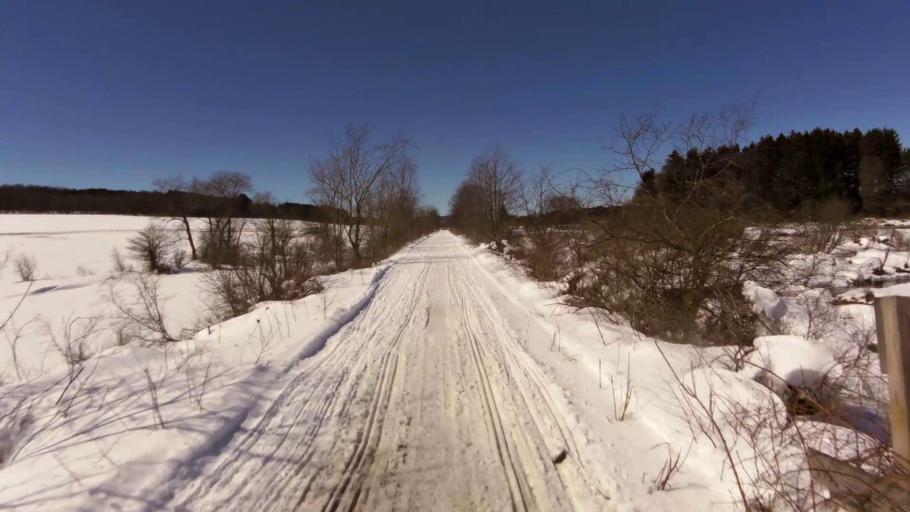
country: US
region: New York
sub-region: Cattaraugus County
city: Delevan
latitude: 42.4324
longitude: -78.3983
